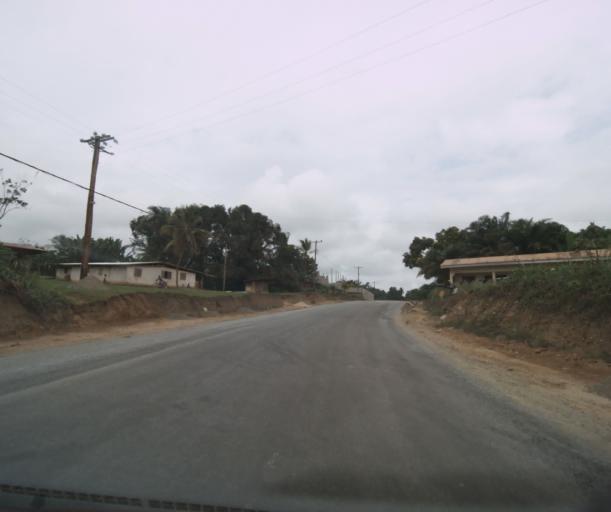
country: CM
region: South Province
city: Kribi
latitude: 2.9073
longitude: 9.9058
